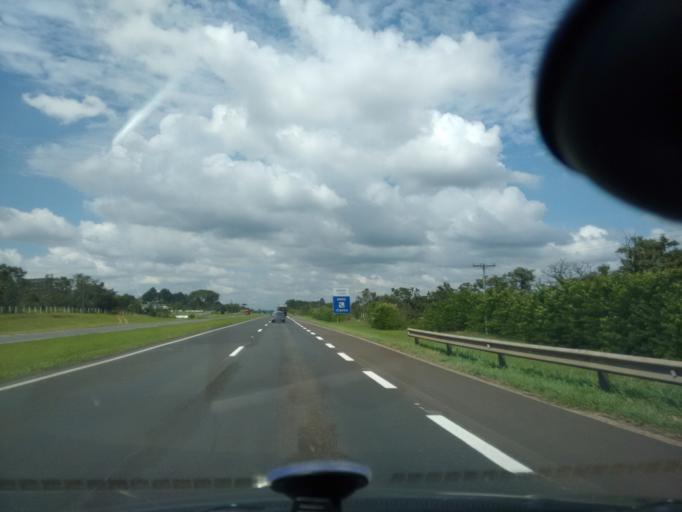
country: BR
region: Sao Paulo
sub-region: Sao Carlos
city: Sao Carlos
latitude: -22.0759
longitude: -47.8423
